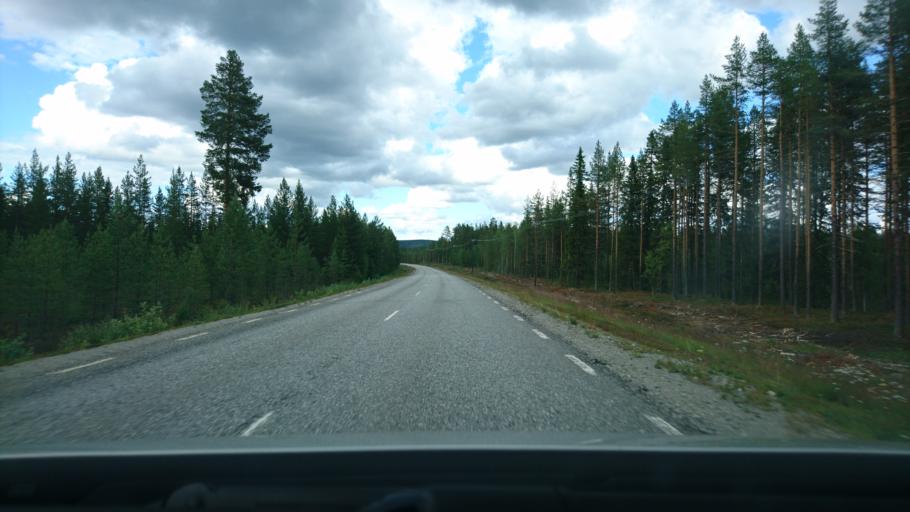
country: SE
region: Vaesterbotten
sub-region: Asele Kommun
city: Asele
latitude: 63.9185
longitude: 17.2448
